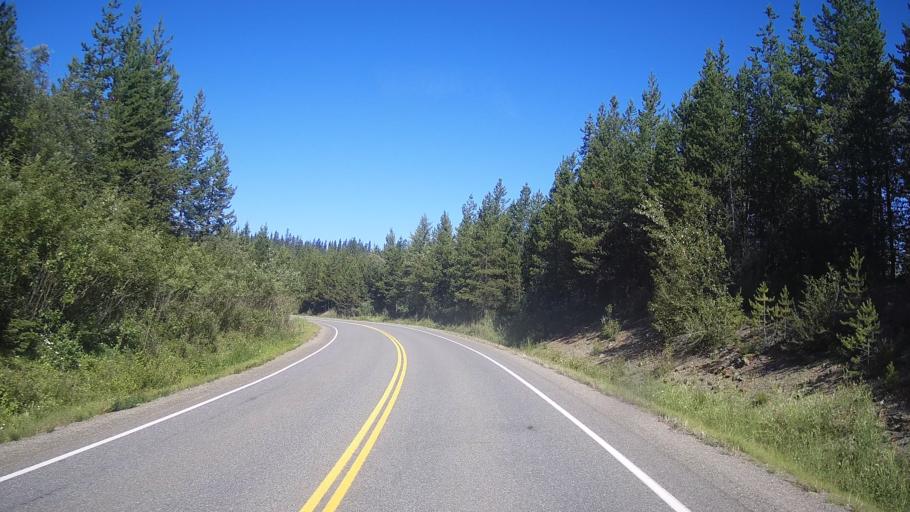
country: CA
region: British Columbia
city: Kamloops
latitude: 51.5032
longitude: -120.3492
